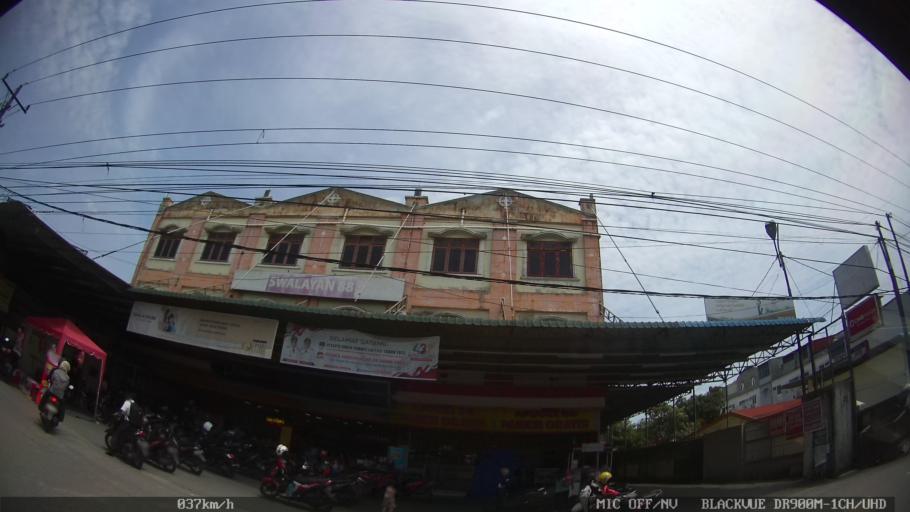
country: ID
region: North Sumatra
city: Sunggal
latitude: 3.5775
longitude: 98.6229
